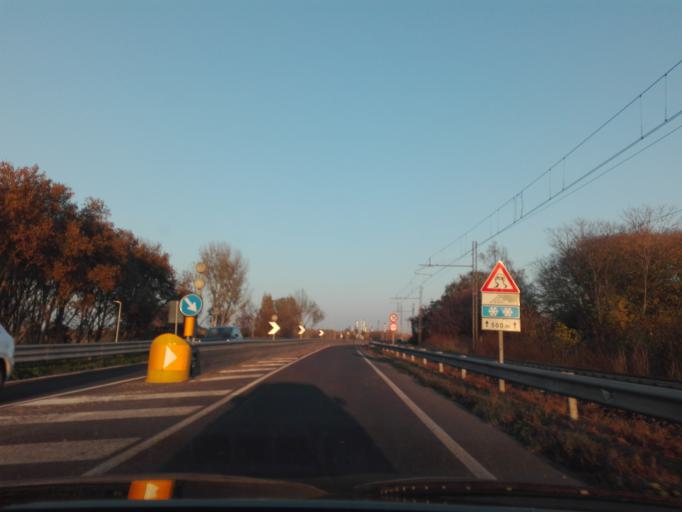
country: IT
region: Lombardy
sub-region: Provincia di Mantova
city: Mantova
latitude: 45.1443
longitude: 10.8047
